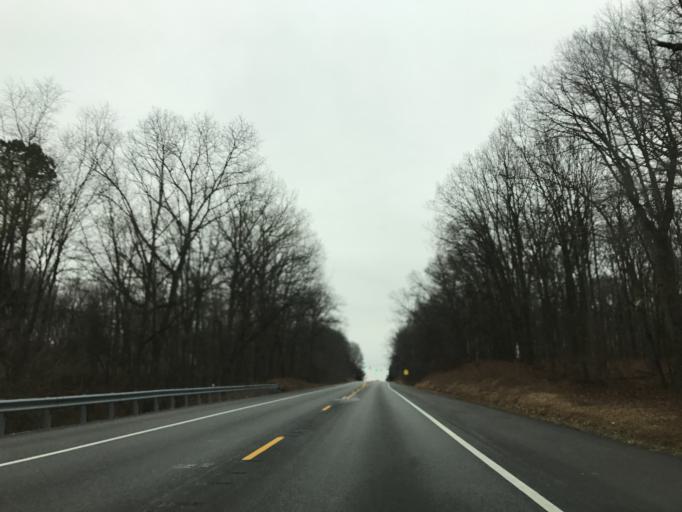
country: US
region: Maryland
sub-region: Carroll County
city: Taneytown
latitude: 39.6310
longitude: -77.1104
